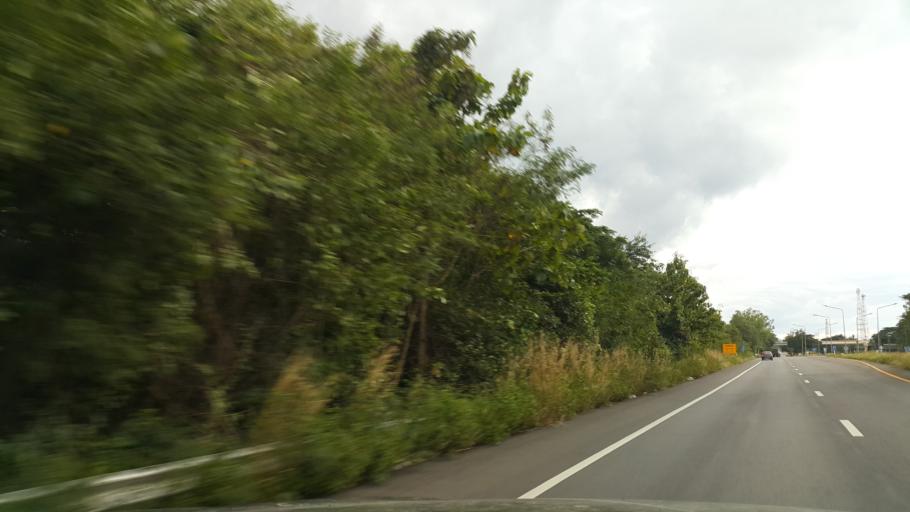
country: TH
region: Lampang
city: Sop Prap
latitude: 17.8003
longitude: 99.2669
